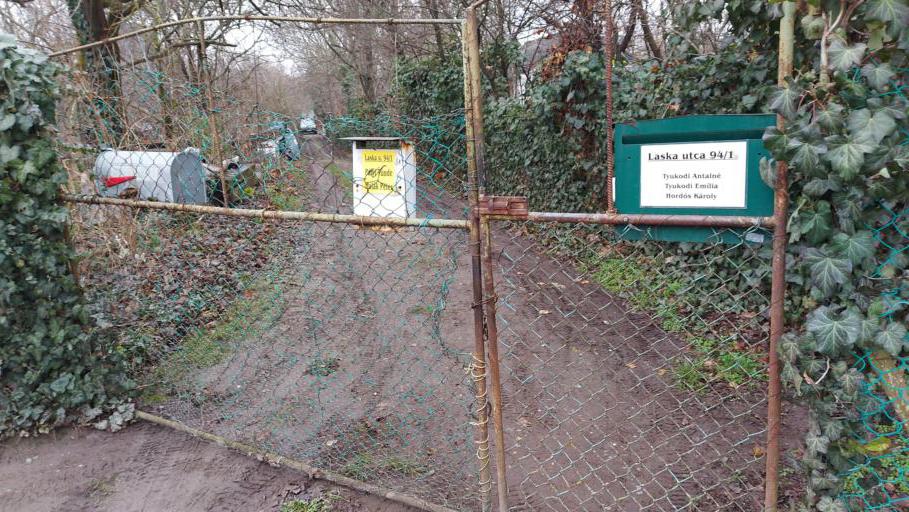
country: HU
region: Budapest
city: Budapest XXII. keruelet
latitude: 47.4350
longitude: 19.0003
